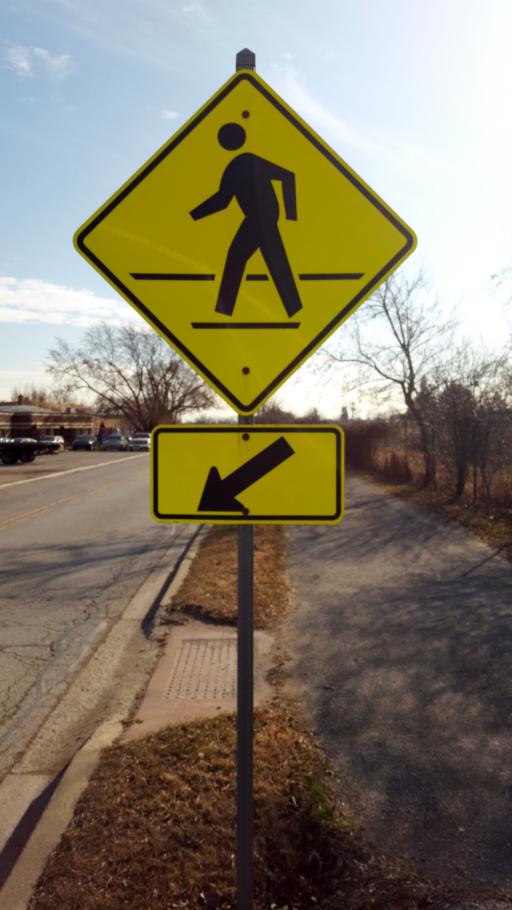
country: US
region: Illinois
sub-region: Cook County
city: Northfield
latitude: 42.0945
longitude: -87.8142
